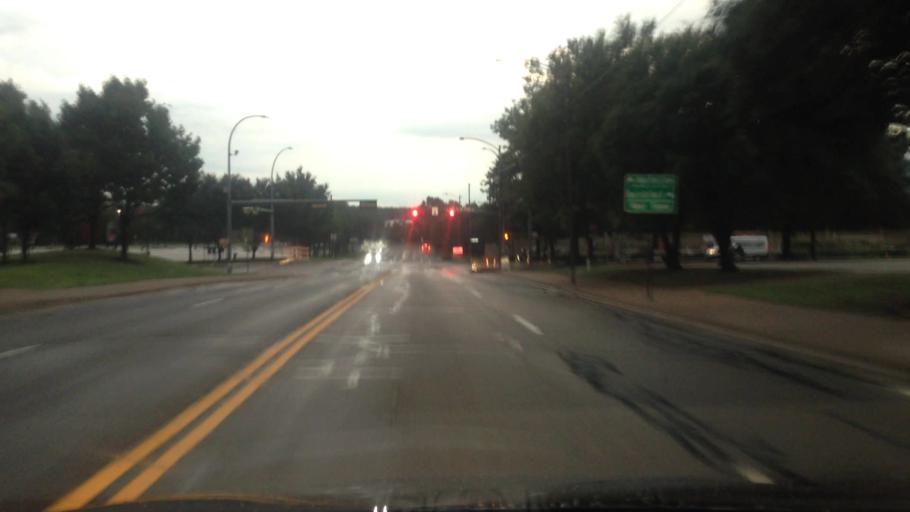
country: US
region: Texas
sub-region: Tarrant County
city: Arlington
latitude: 32.7563
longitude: -97.0887
